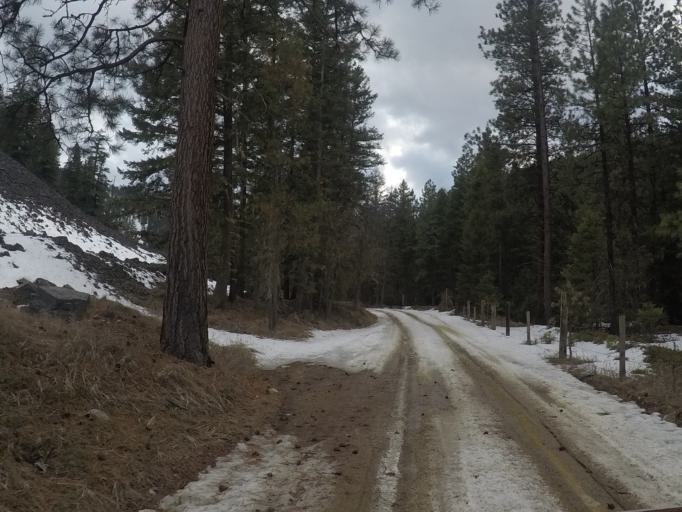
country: US
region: Montana
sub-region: Missoula County
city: Clinton
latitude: 46.5783
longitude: -113.6812
